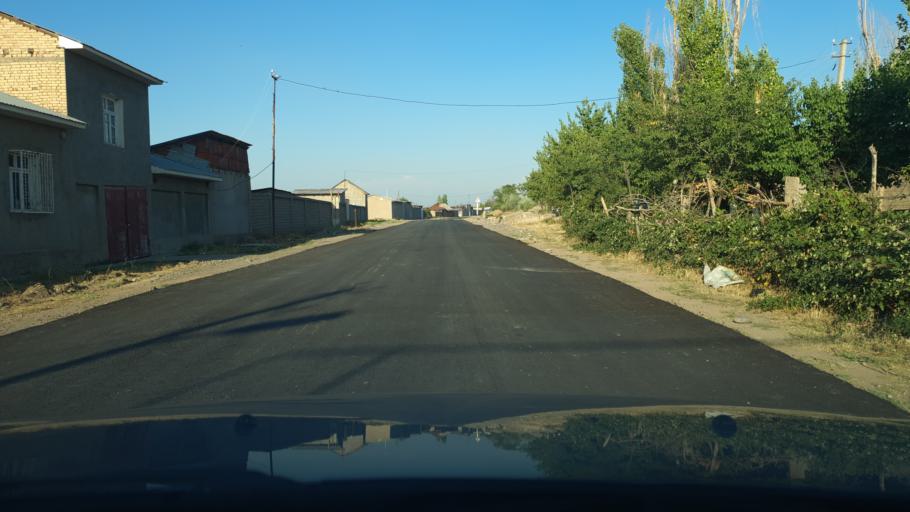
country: UZ
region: Toshkent
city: Salor
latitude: 41.4566
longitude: 69.3991
